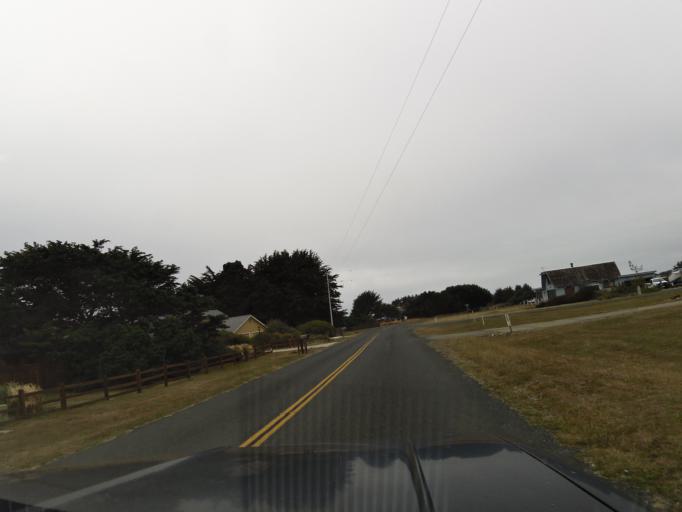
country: US
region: California
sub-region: Mendocino County
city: Fort Bragg
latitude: 39.3577
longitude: -123.8212
